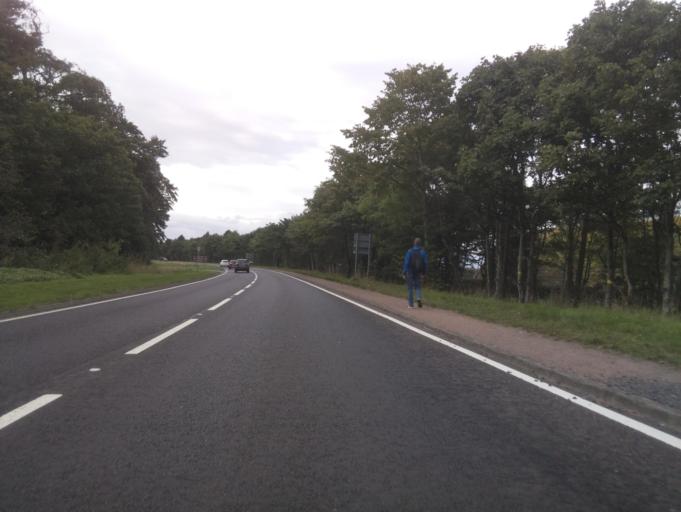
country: GB
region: Scotland
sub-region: Fife
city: Saint Andrews
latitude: 56.3463
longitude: -2.8194
